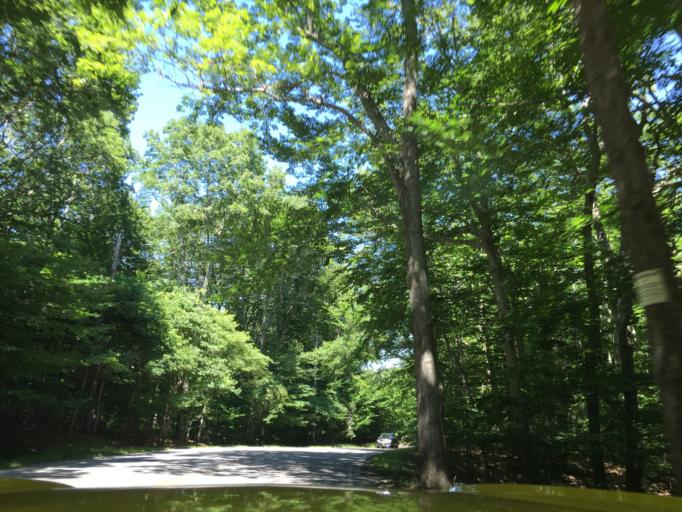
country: US
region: New York
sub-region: Suffolk County
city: Amagansett
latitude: 40.9945
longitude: -72.1343
